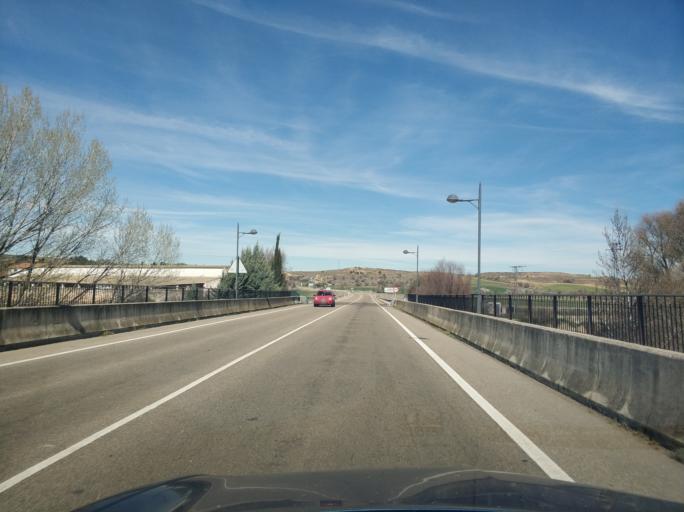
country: ES
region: Castille and Leon
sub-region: Provincia de Valladolid
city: Simancas
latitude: 41.5897
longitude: -4.8181
